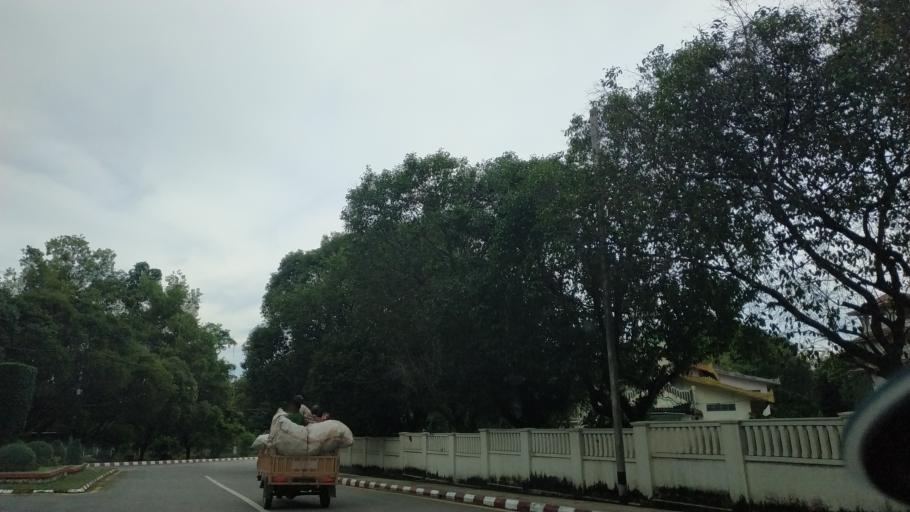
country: MM
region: Tanintharyi
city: Dawei
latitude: 14.0767
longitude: 98.2093
